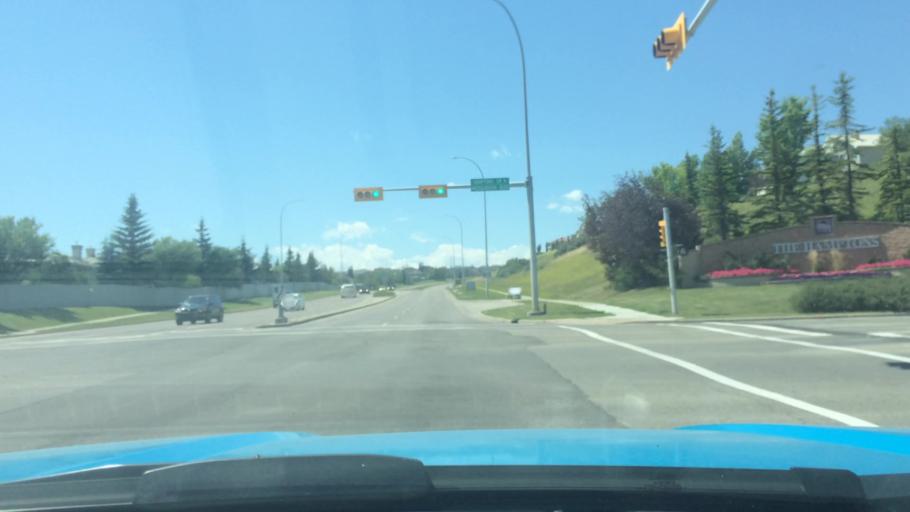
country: CA
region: Alberta
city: Calgary
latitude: 51.1405
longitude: -114.1318
